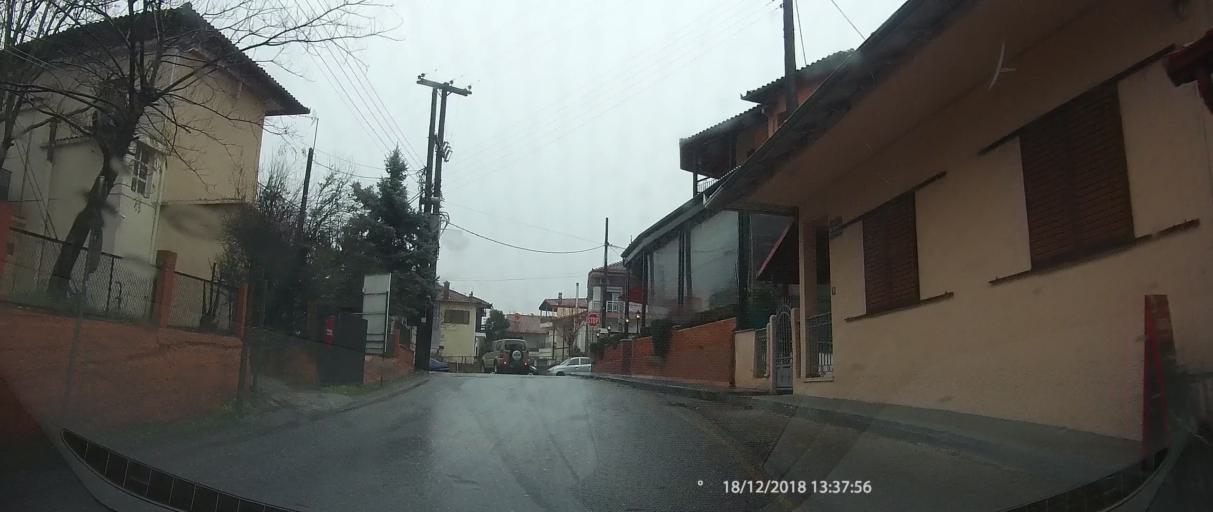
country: GR
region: Central Macedonia
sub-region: Nomos Pierias
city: Litochoro
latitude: 40.1058
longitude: 22.5029
